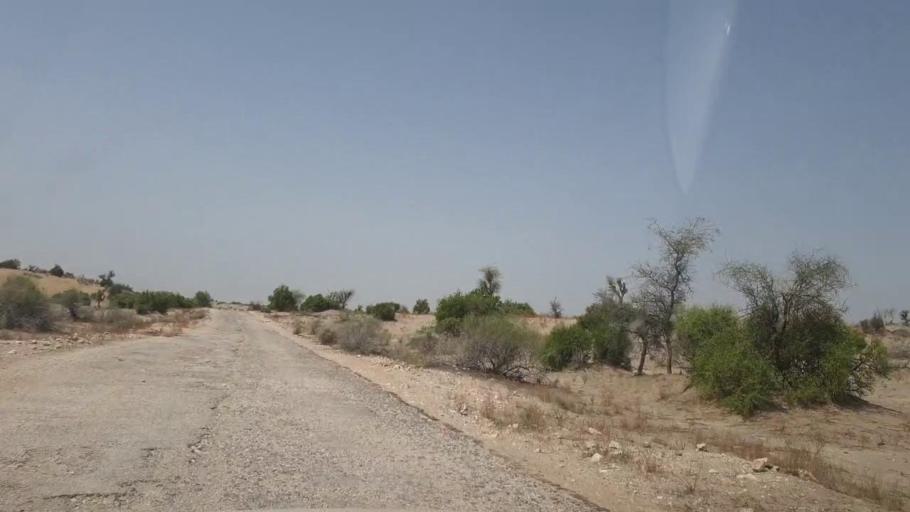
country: PK
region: Sindh
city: Khanpur
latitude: 27.3678
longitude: 69.3173
